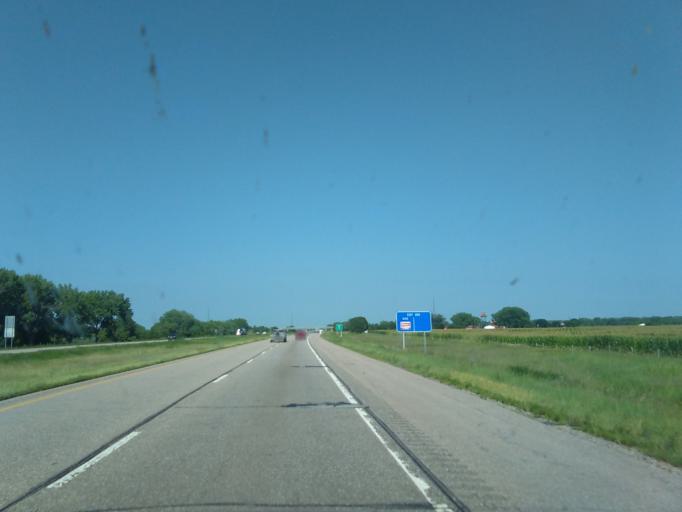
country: US
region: Nebraska
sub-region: Hall County
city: Wood River
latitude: 40.7596
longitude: -98.5983
